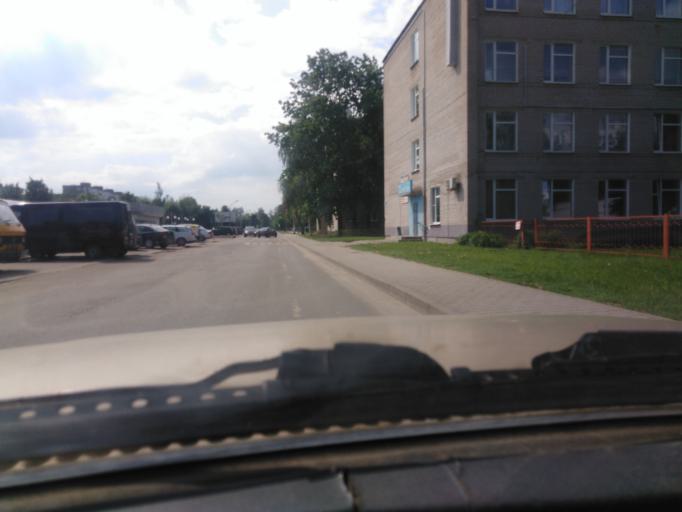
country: BY
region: Mogilev
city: Mahilyow
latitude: 53.9322
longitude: 30.3620
